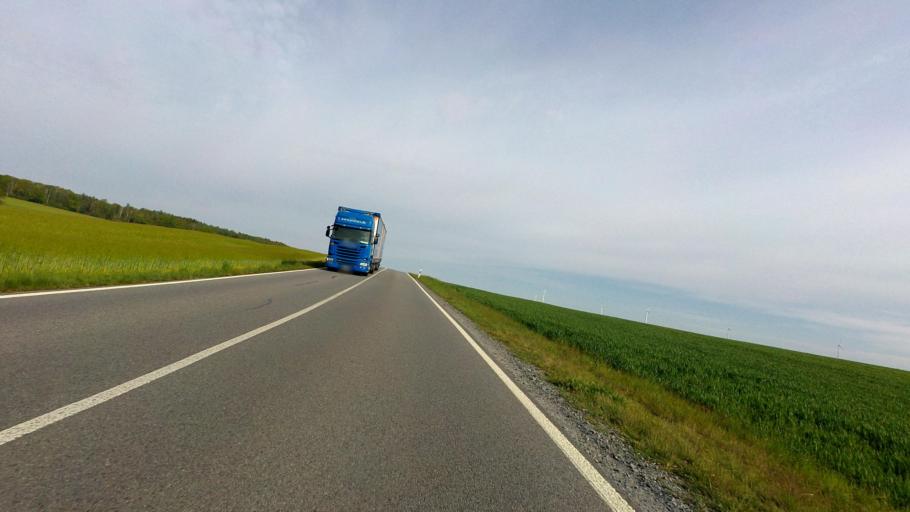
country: DE
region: Saxony
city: Stolpen
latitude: 51.0618
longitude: 14.0589
